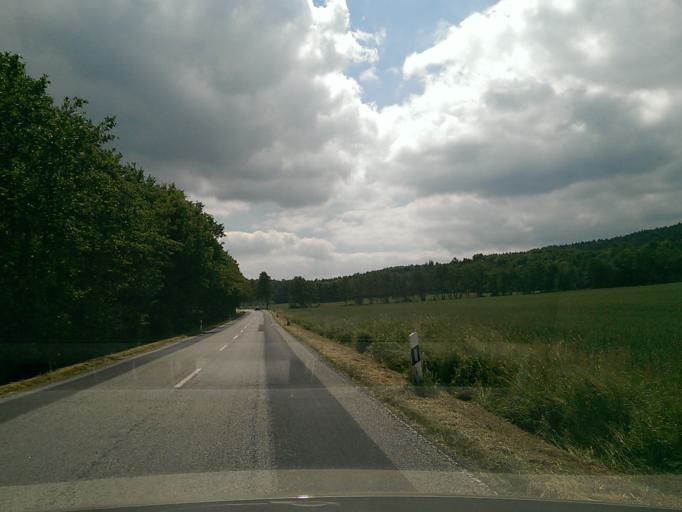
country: DE
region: Saxony
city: Kurort Jonsdorf
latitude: 50.8681
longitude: 14.6884
